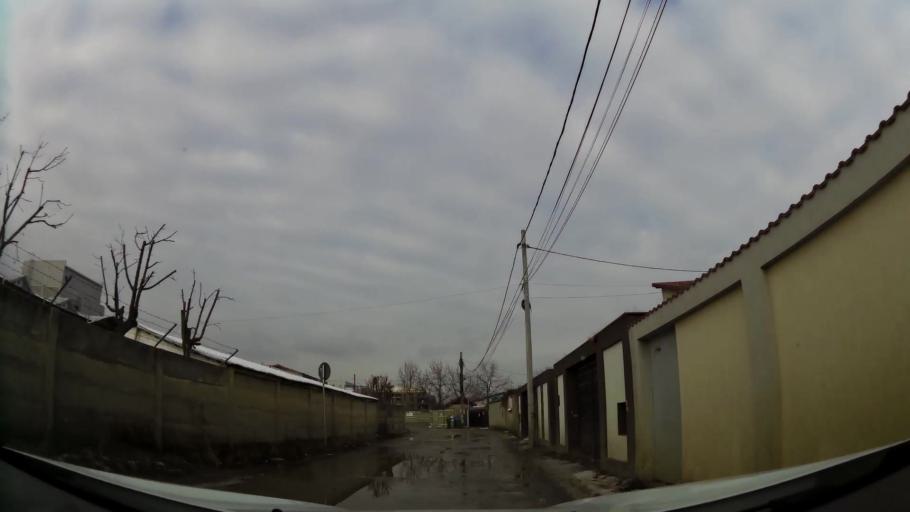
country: RO
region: Ilfov
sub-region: Comuna Popesti-Leordeni
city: Popesti-Leordeni
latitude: 44.4052
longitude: 26.1859
